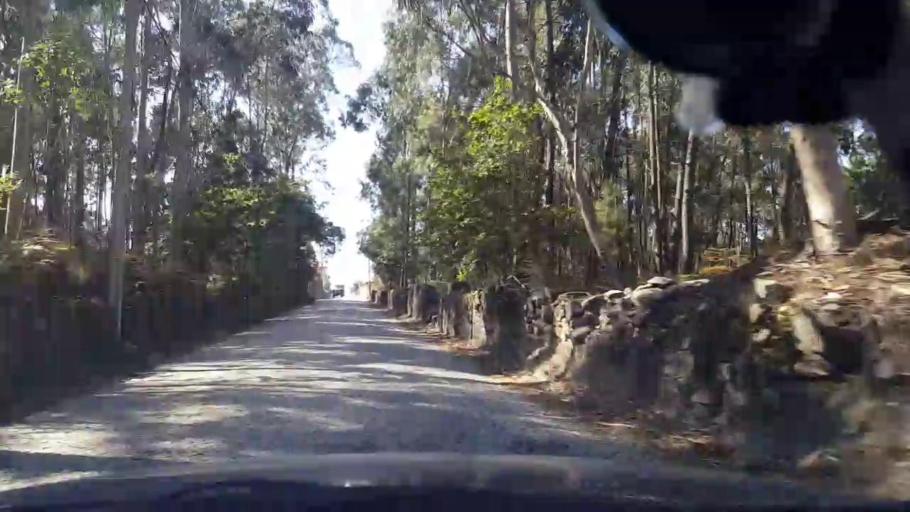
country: PT
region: Porto
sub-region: Povoa de Varzim
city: Pedroso
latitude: 41.4026
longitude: -8.6967
